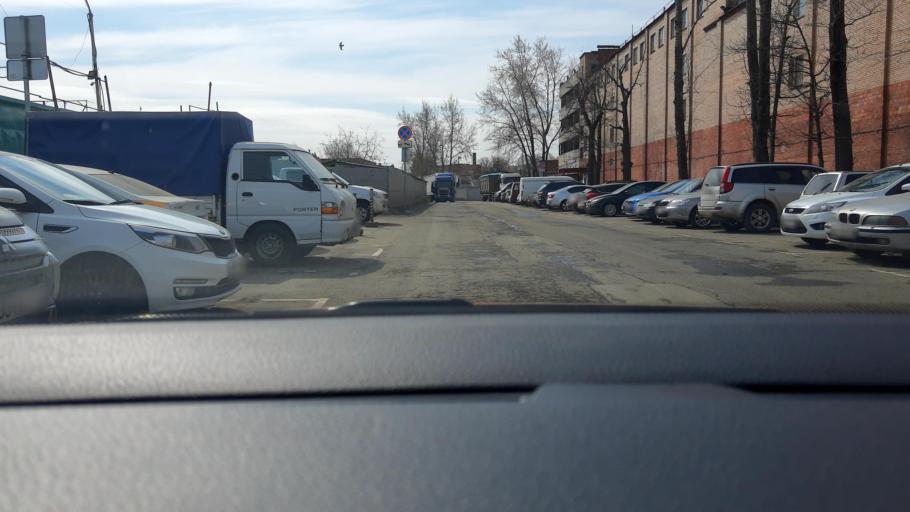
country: RU
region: Moscow
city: Vagonoremont
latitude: 55.8940
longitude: 37.5514
